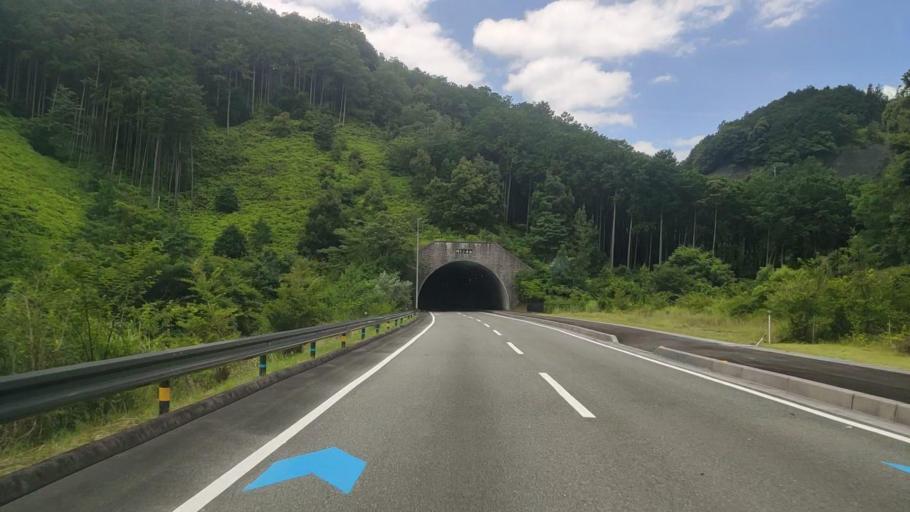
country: JP
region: Mie
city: Owase
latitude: 34.2345
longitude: 136.3984
